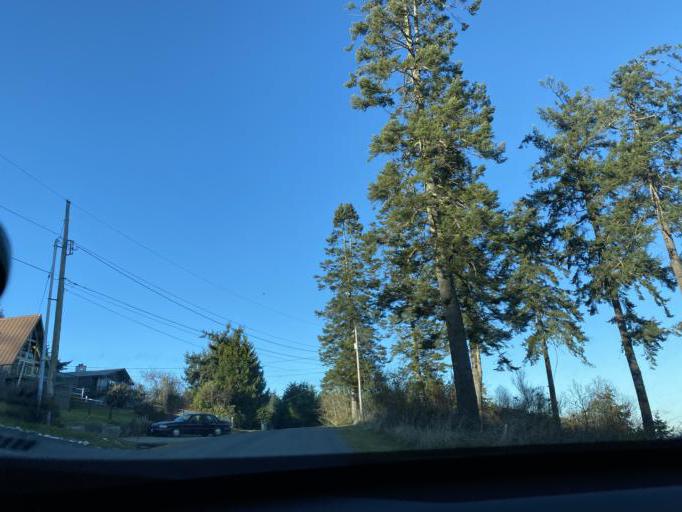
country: US
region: Washington
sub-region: Island County
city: Camano
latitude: 48.1295
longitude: -122.5649
